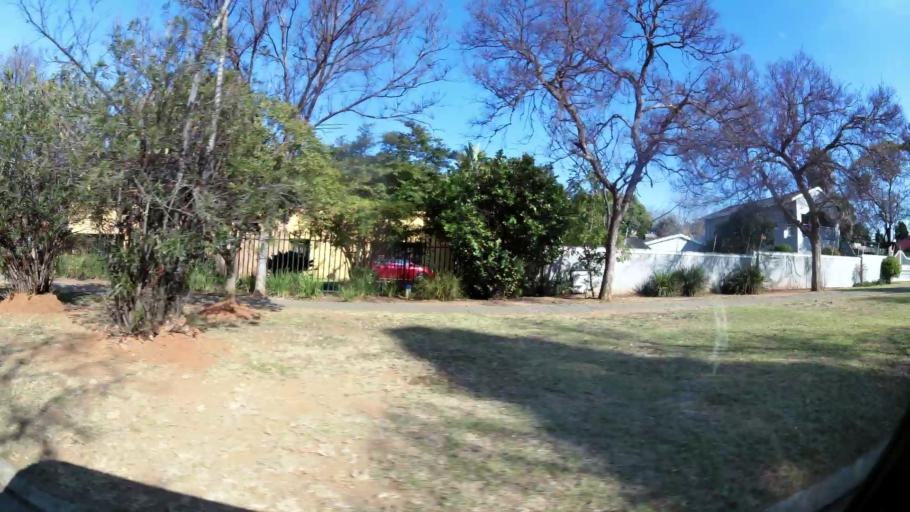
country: ZA
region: Gauteng
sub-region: City of Johannesburg Metropolitan Municipality
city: Roodepoort
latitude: -26.1099
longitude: 27.9537
